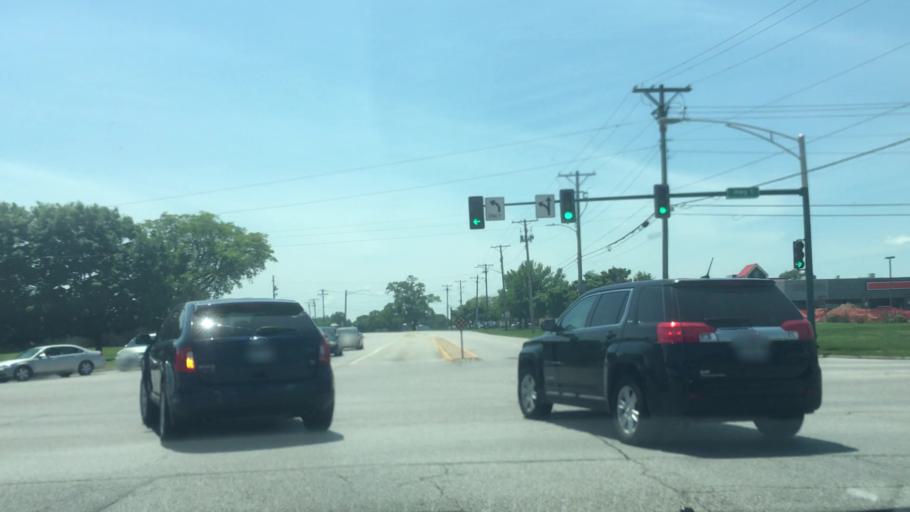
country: US
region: Iowa
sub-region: Johnson County
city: Iowa City
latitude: 41.6476
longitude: -91.5401
